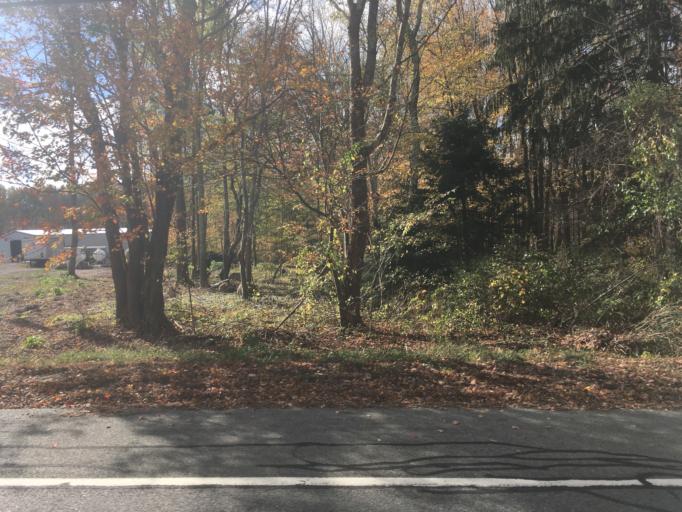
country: US
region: Rhode Island
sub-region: Providence County
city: Chepachet
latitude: 41.8426
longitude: -71.6778
